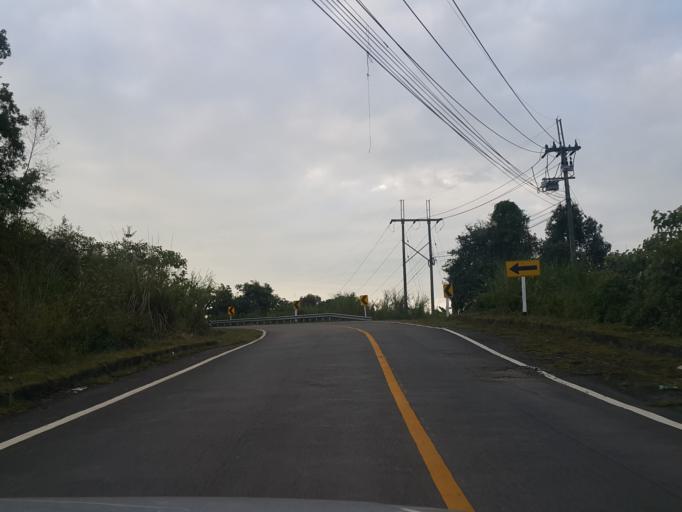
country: TH
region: Mae Hong Son
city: Khun Yuam
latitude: 18.7994
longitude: 98.0680
